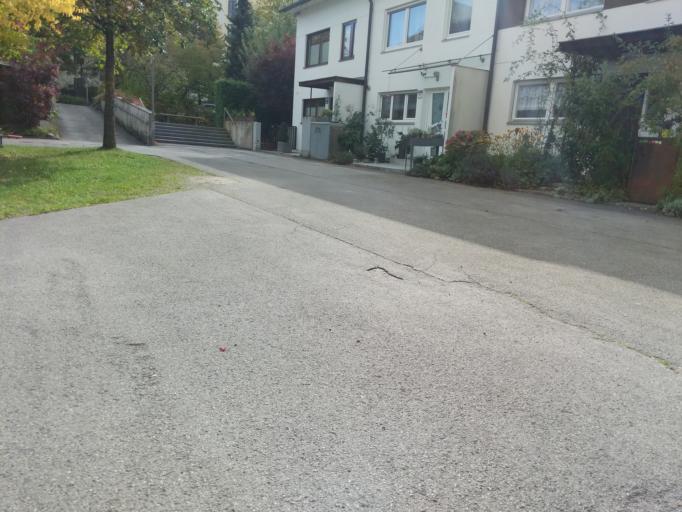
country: DE
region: Bavaria
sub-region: Upper Bavaria
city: Zorneding
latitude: 48.0864
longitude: 11.8349
